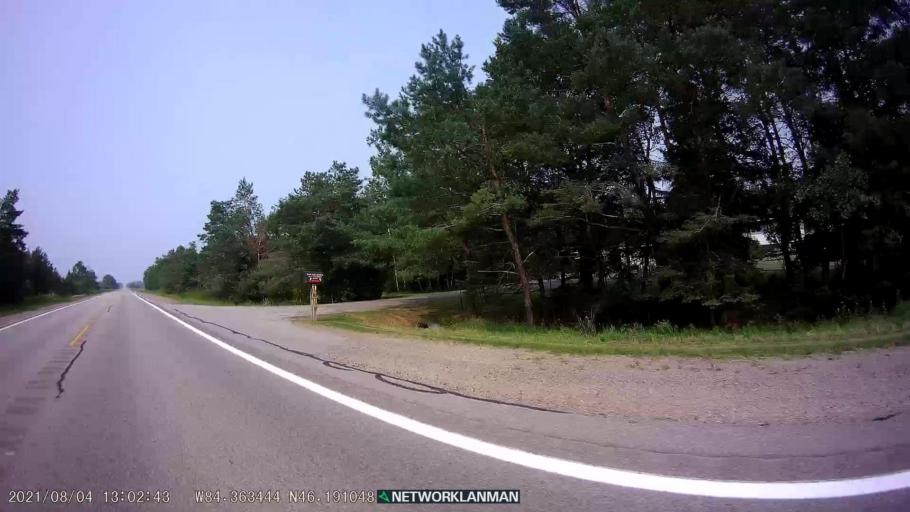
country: US
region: Michigan
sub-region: Chippewa County
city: Sault Ste. Marie
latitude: 46.1926
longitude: -84.3634
